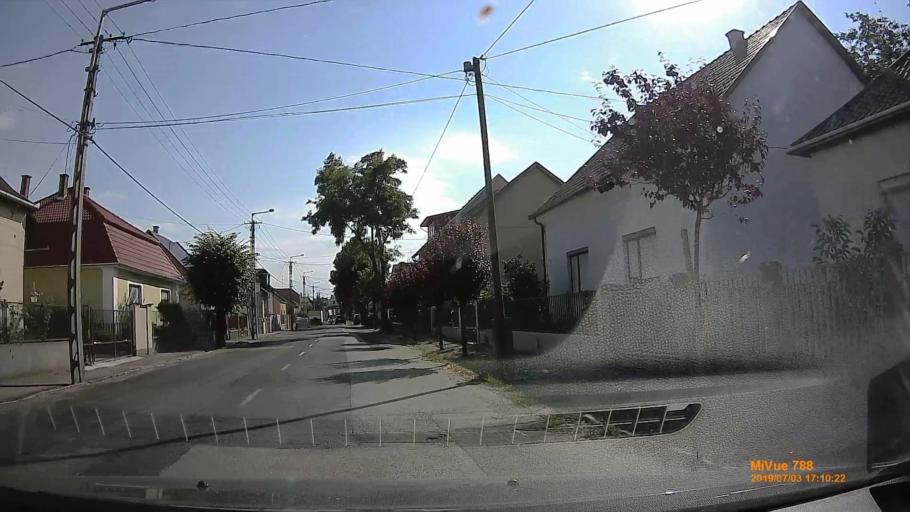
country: HU
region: Gyor-Moson-Sopron
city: Gyor
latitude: 47.7035
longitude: 17.6416
